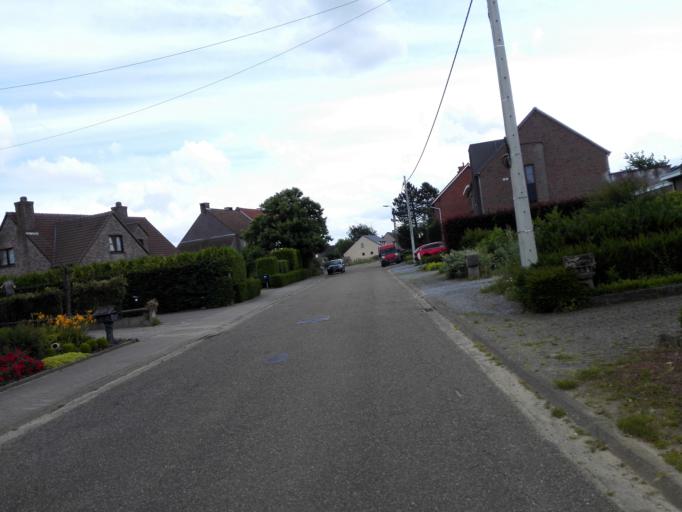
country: BE
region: Flanders
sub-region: Provincie Vlaams-Brabant
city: Bierbeek
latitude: 50.8486
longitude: 4.7871
